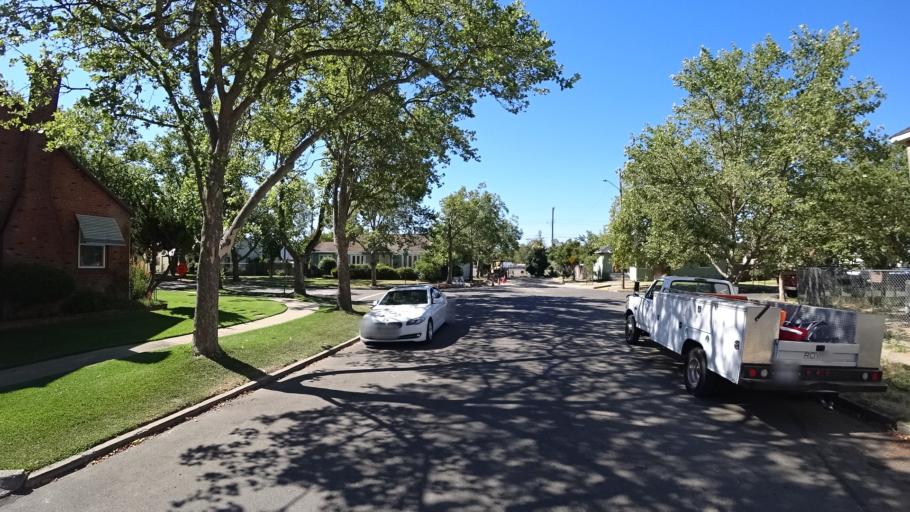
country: US
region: California
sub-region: Sacramento County
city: Parkway
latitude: 38.5314
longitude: -121.4433
